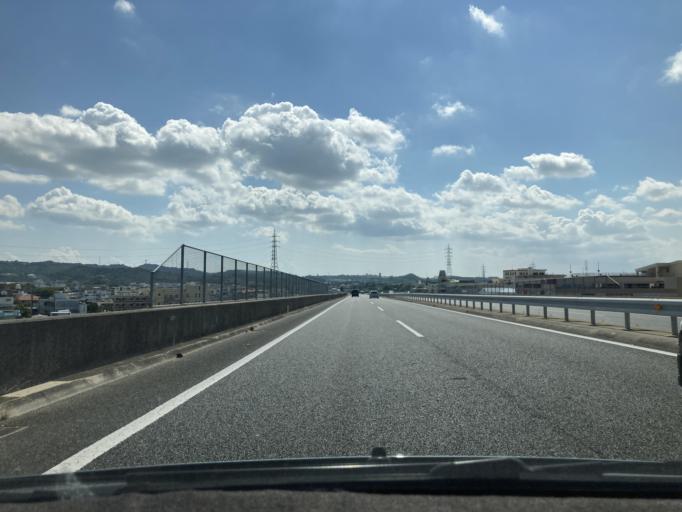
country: JP
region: Okinawa
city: Naha-shi
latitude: 26.2029
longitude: 127.7389
